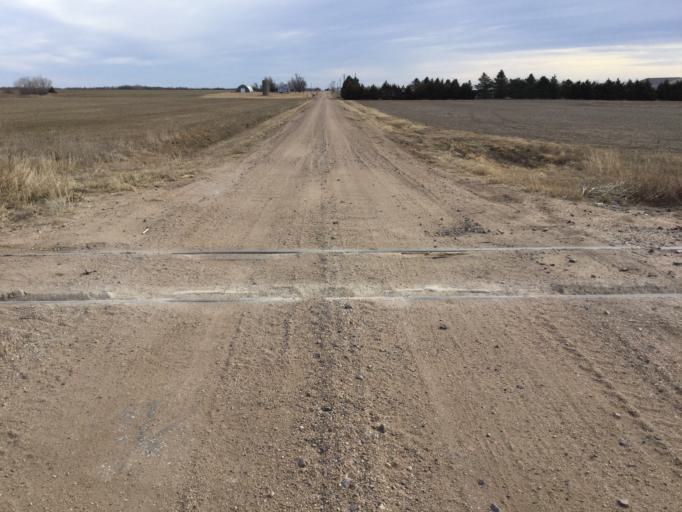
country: US
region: Kansas
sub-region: Rice County
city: Lyons
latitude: 38.4788
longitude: -98.1923
